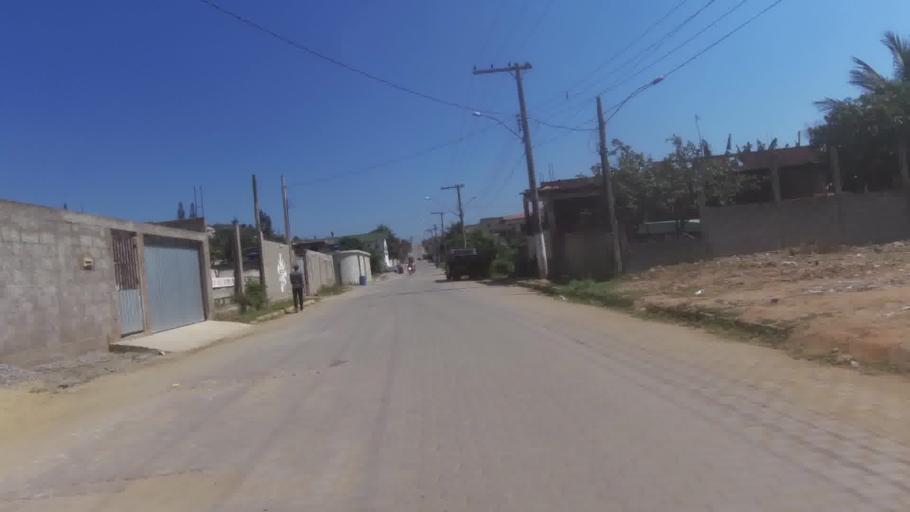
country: BR
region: Espirito Santo
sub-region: Itapemirim
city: Itapemirim
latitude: -21.0173
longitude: -40.8172
